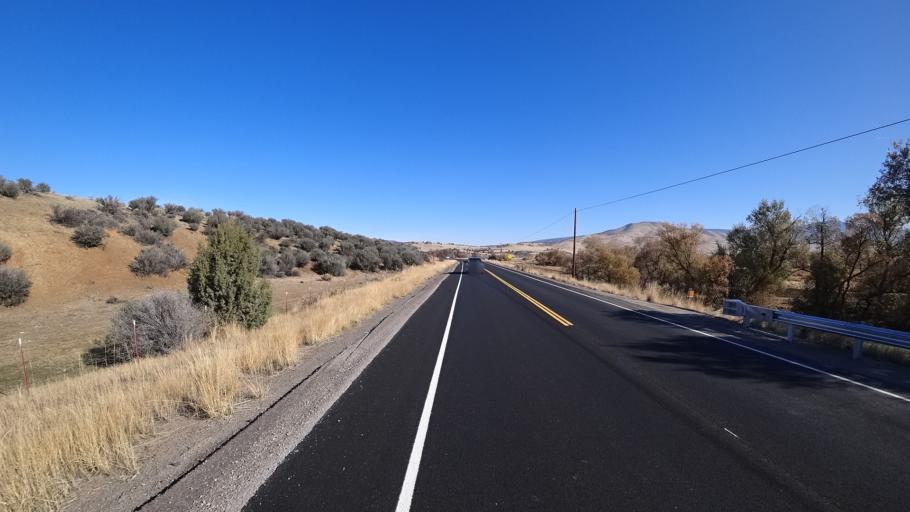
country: US
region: California
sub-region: Siskiyou County
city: Montague
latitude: 41.8413
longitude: -122.4780
